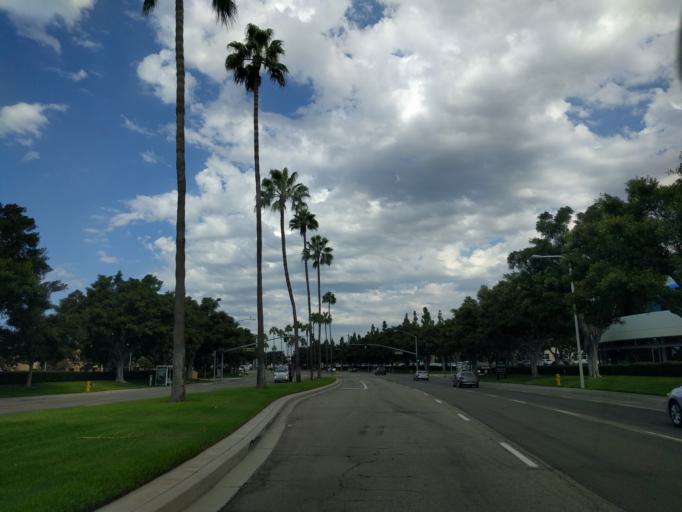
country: US
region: California
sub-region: Orange County
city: Laguna Woods
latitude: 33.6534
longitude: -117.7368
